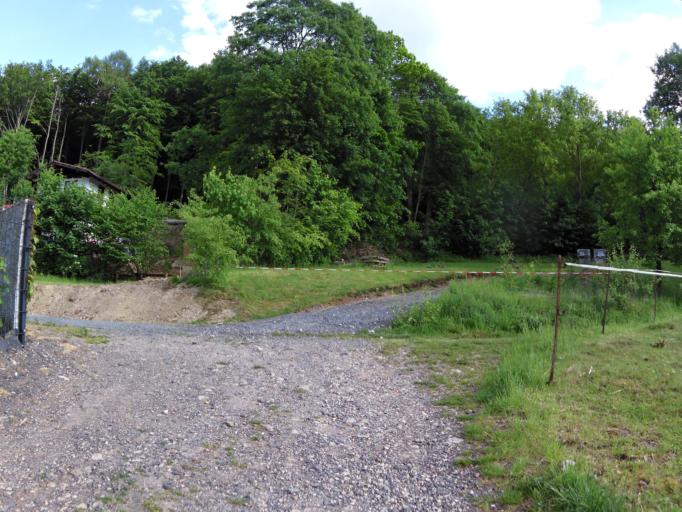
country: DE
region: Thuringia
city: Dermbach
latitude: 50.7112
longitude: 10.1095
